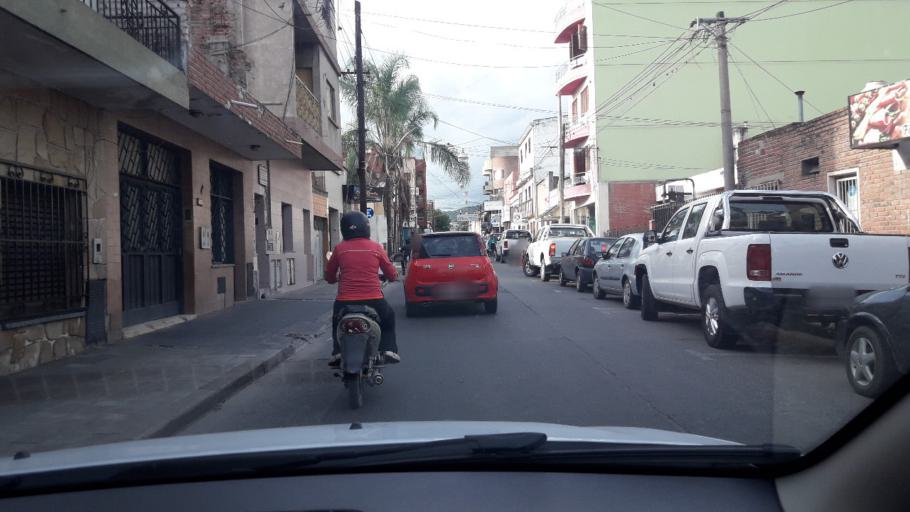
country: AR
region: Jujuy
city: San Salvador de Jujuy
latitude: -24.1905
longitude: -65.2988
